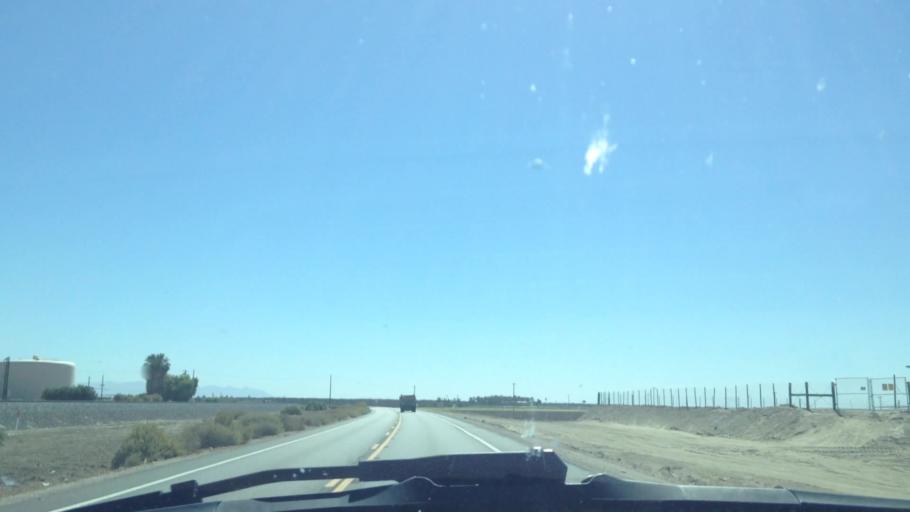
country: US
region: California
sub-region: Riverside County
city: Mecca
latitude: 33.5401
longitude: -116.0299
